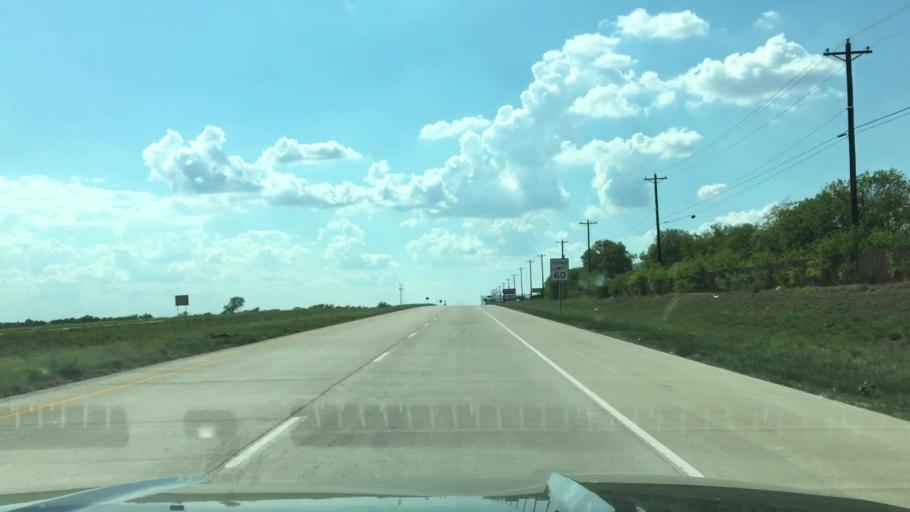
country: US
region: Texas
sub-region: Tarrant County
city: Haslet
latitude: 33.0359
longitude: -97.3777
